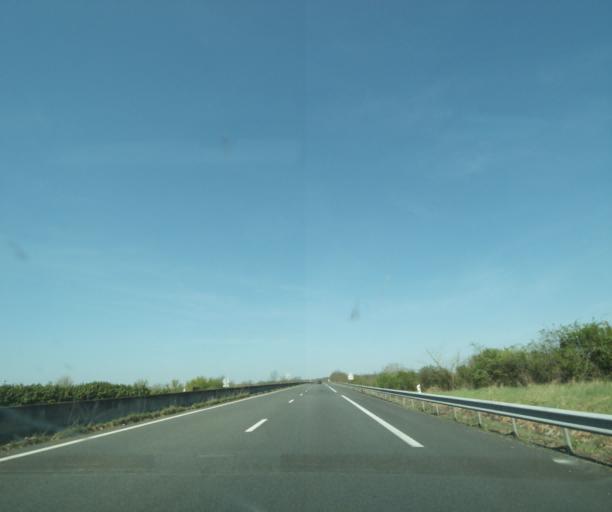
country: FR
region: Bourgogne
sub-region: Departement de la Nievre
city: Pouilly-sur-Loire
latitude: 47.2769
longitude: 2.9749
